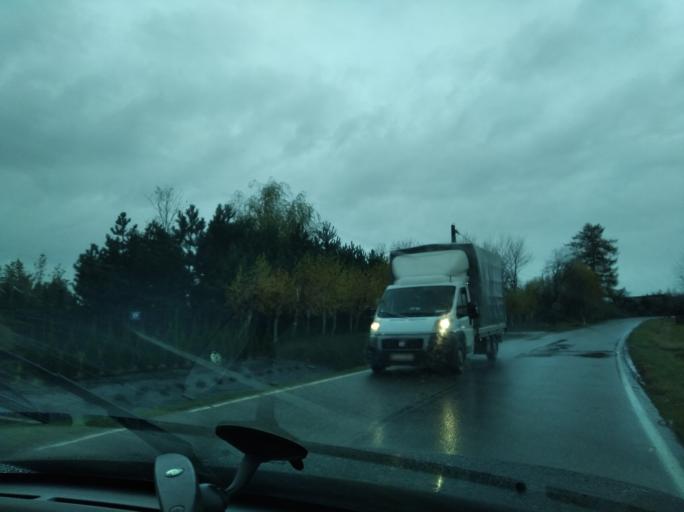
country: PL
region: Subcarpathian Voivodeship
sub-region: Powiat lancucki
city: Handzlowka
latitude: 49.9898
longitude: 22.1891
